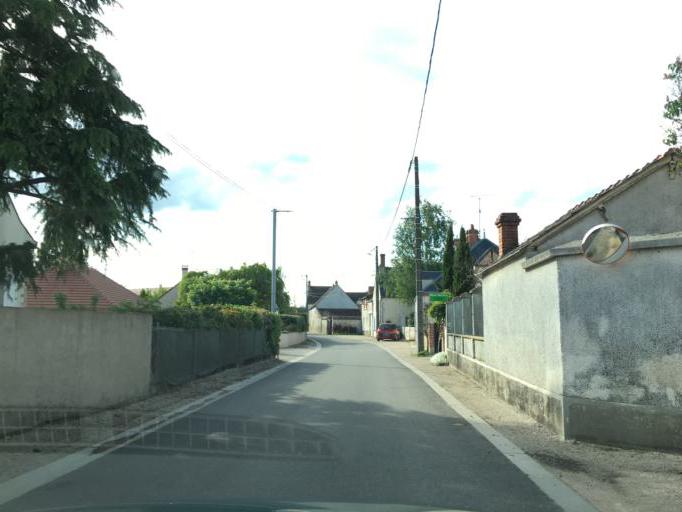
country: FR
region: Centre
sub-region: Departement du Loiret
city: Saint-Hilaire-Saint-Mesmin
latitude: 47.8415
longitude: 1.8117
